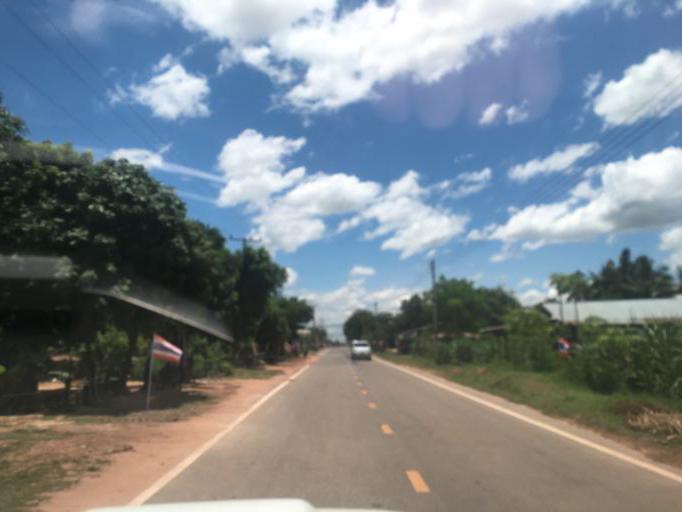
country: TH
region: Changwat Udon Thani
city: Nong Saeng
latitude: 17.1365
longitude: 102.7865
